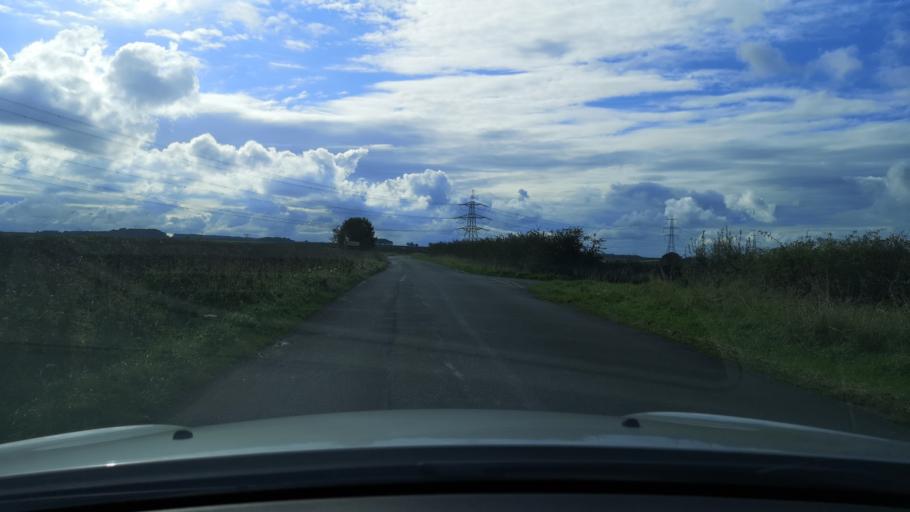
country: GB
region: England
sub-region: East Riding of Yorkshire
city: Walkington
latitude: 53.8305
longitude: -0.5015
